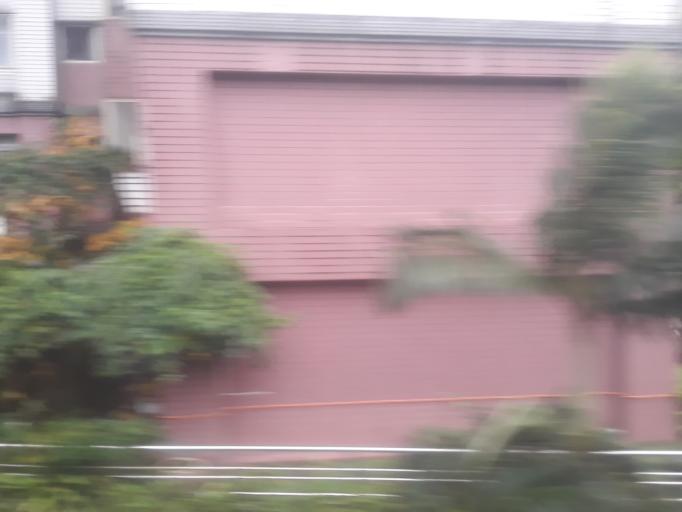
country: TW
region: Taipei
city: Taipei
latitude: 24.9972
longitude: 121.5625
